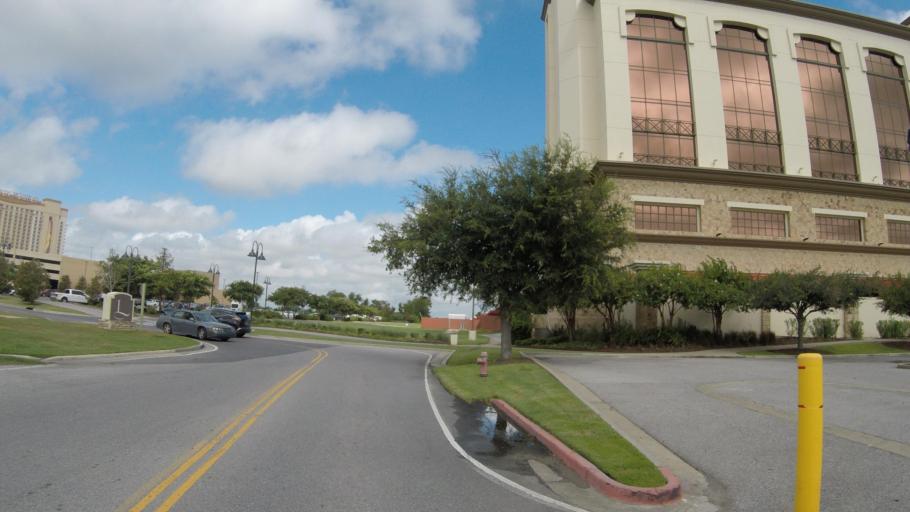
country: US
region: Louisiana
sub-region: Calcasieu Parish
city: Prien
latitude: 30.2051
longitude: -93.2596
